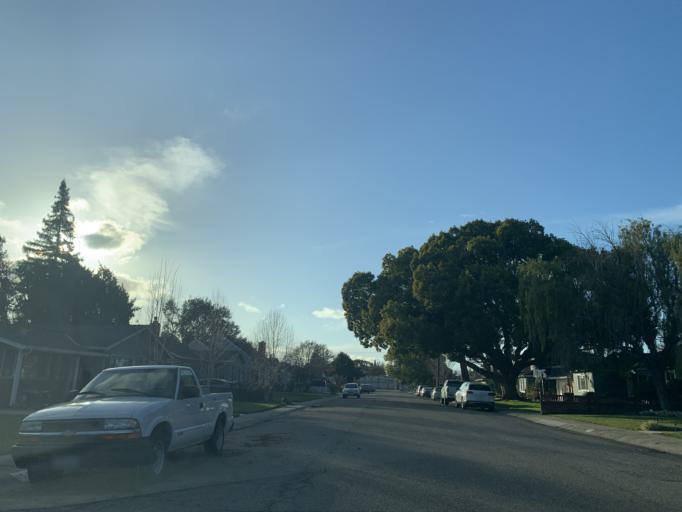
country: US
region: California
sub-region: Santa Clara County
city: Buena Vista
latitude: 37.3019
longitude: -121.9112
